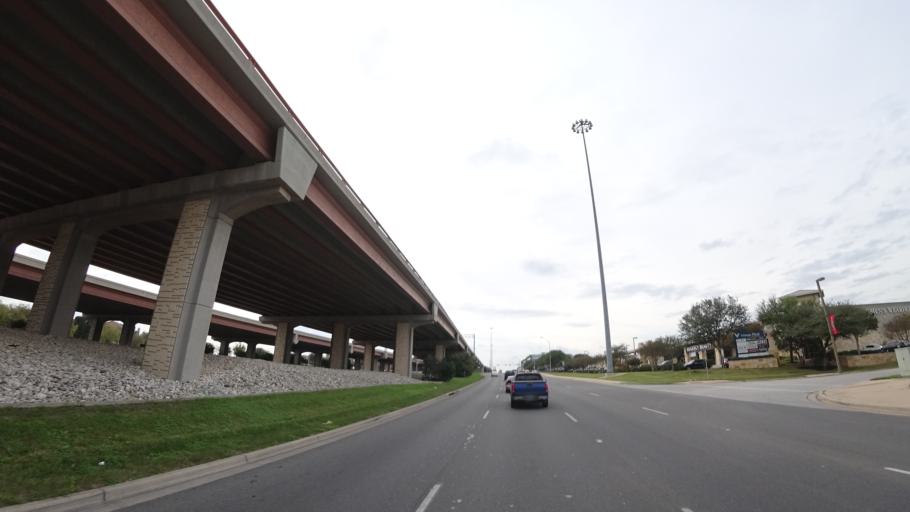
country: US
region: Texas
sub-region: Williamson County
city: Round Rock
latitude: 30.4802
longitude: -97.6824
